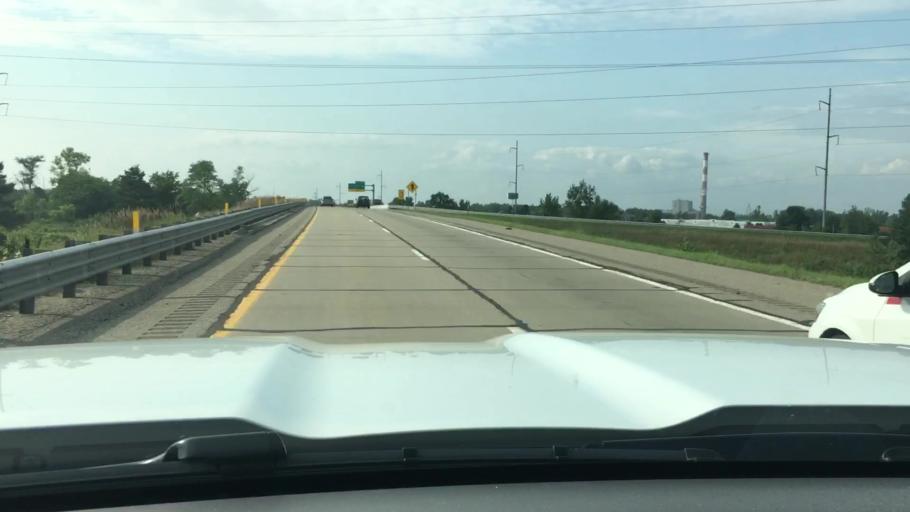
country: US
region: Michigan
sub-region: Eaton County
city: Dimondale
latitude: 42.6759
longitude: -84.6501
